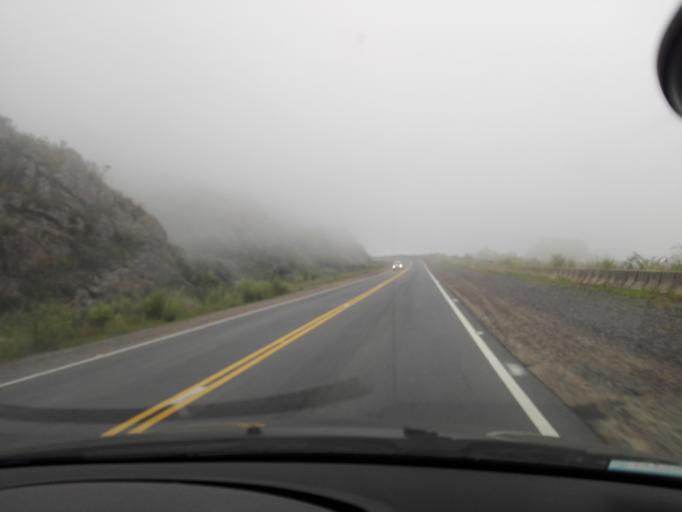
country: AR
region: Cordoba
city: Cuesta Blanca
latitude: -31.6028
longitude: -64.7030
